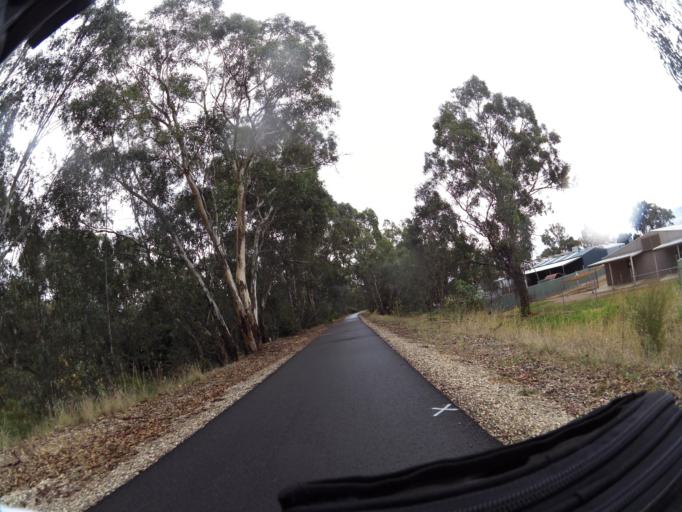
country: AU
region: Victoria
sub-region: Wodonga
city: Wodonga
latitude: -36.1336
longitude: 146.8999
